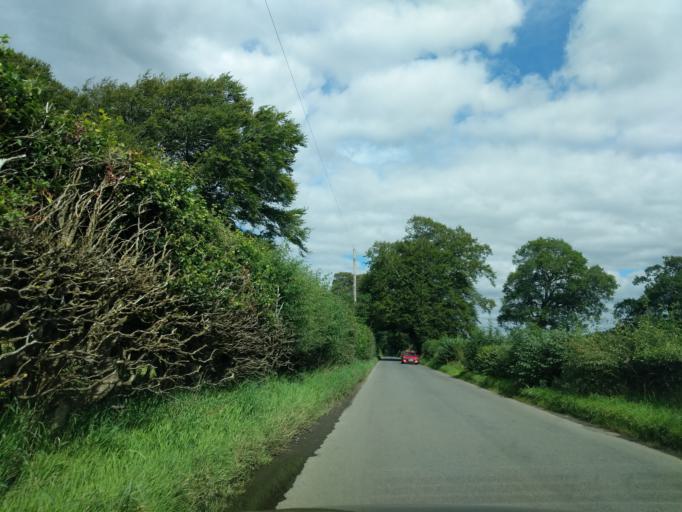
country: GB
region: Scotland
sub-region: The Scottish Borders
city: Peebles
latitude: 55.6269
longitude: -3.2957
